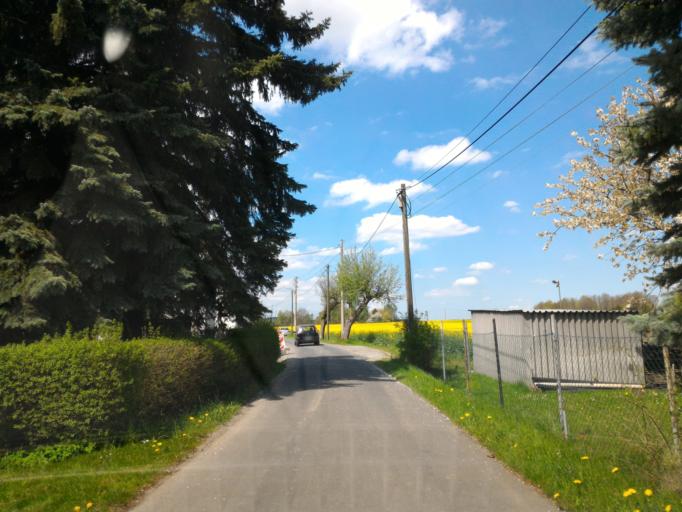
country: DE
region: Saxony
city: Leutersdorf
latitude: 50.9505
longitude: 14.6720
